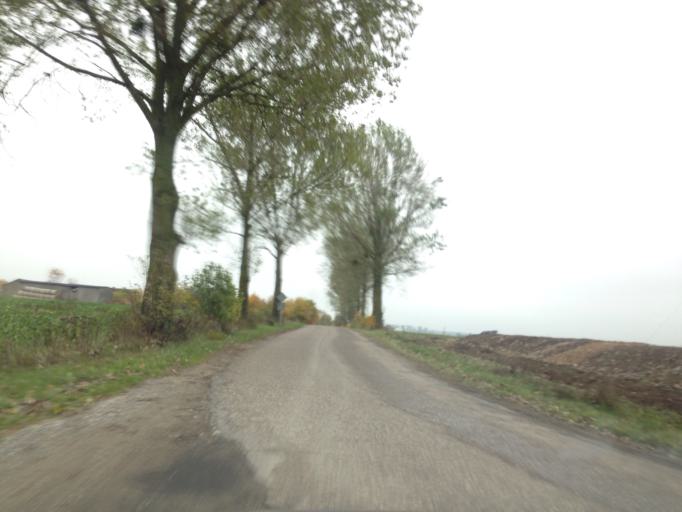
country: PL
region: Kujawsko-Pomorskie
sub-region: Powiat brodnicki
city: Bartniczka
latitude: 53.2099
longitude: 19.5763
